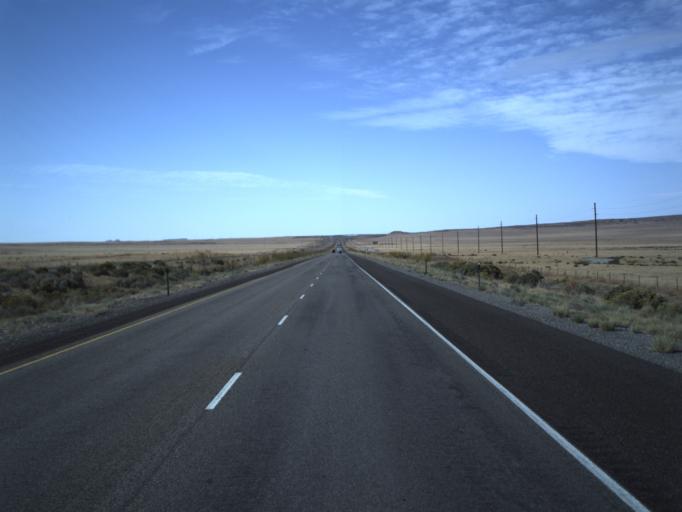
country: US
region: Utah
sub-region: Tooele County
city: Grantsville
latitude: 40.7995
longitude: -112.9442
